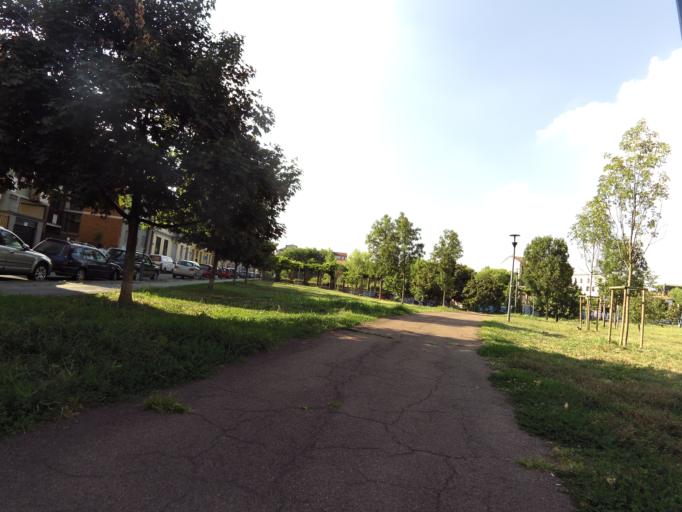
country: IT
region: Lombardy
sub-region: Citta metropolitana di Milano
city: Milano
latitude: 45.4471
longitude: 9.1658
